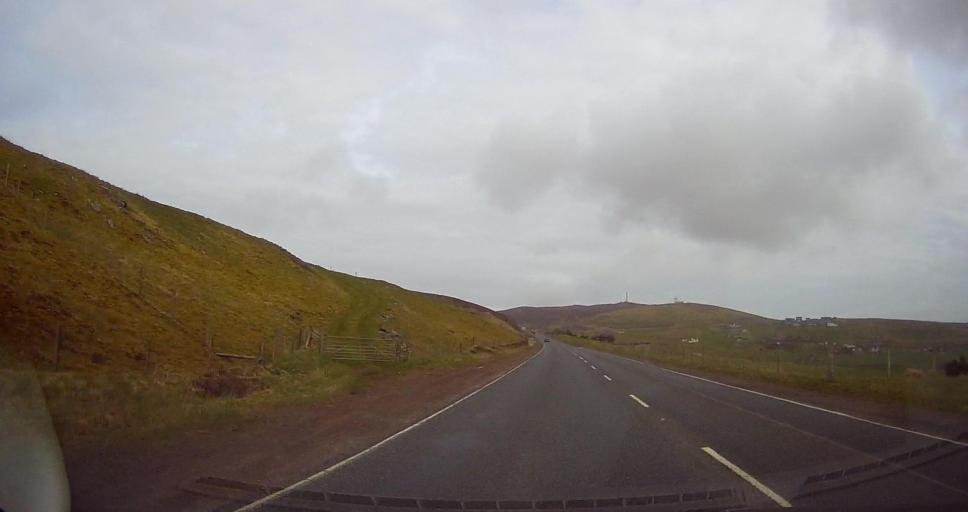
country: GB
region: Scotland
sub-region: Shetland Islands
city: Lerwick
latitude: 60.1287
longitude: -1.2158
